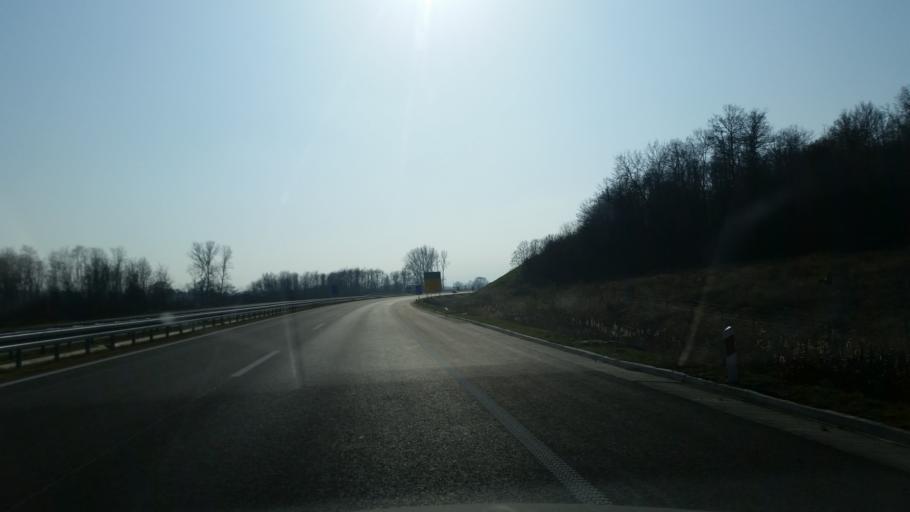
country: RS
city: Prislonica
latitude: 43.9308
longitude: 20.4016
